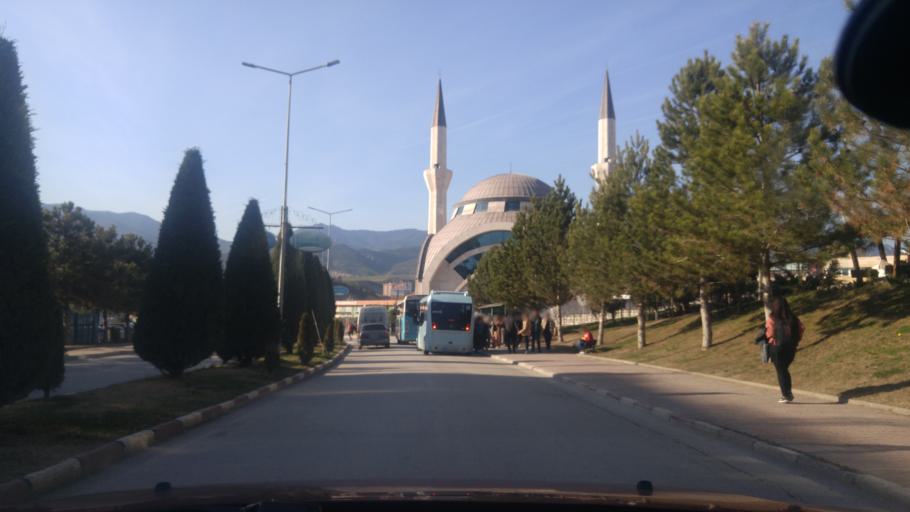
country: TR
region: Karabuk
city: Karabuk
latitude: 41.2110
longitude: 32.6554
